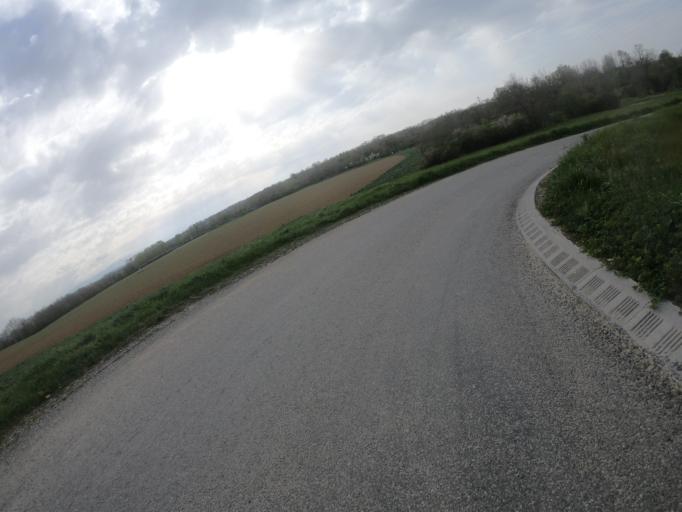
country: FR
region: Languedoc-Roussillon
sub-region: Departement de l'Aude
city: Belpech
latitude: 43.1212
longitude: 1.7399
